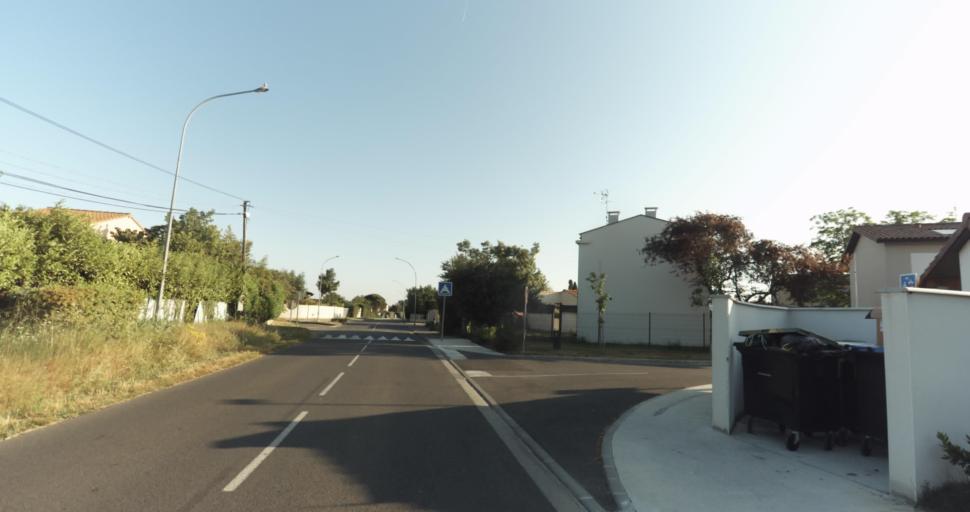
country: FR
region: Midi-Pyrenees
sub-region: Departement de la Haute-Garonne
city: Leguevin
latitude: 43.5923
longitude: 1.2358
